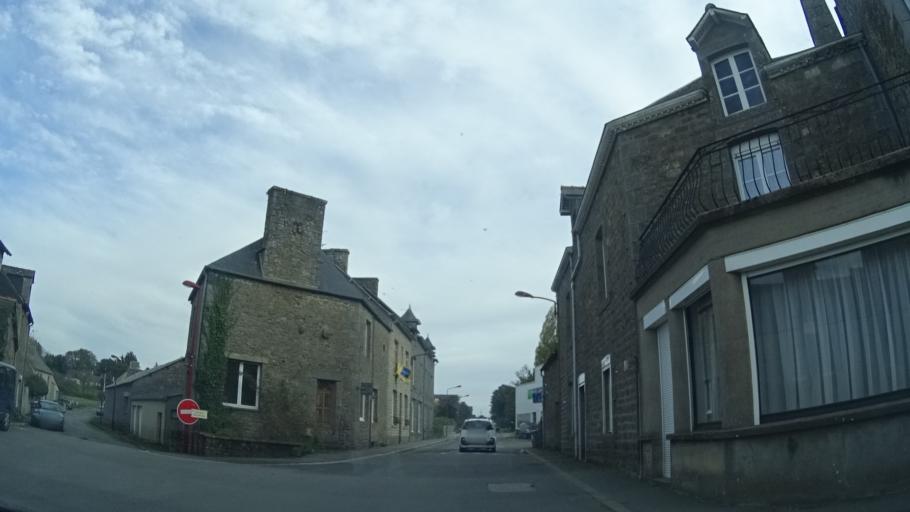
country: FR
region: Brittany
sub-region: Departement d'Ille-et-Vilaine
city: Bonnemain
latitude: 48.4665
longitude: -1.7659
